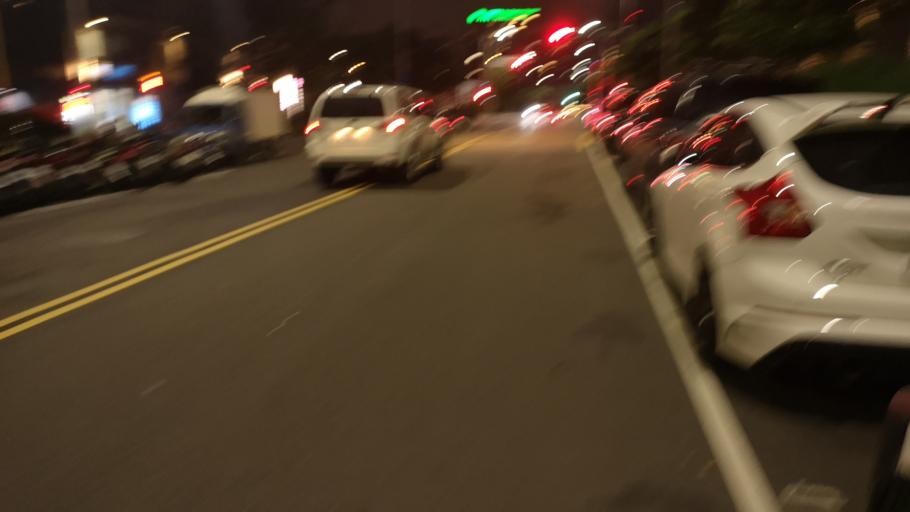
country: TW
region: Taipei
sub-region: Taipei
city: Banqiao
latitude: 24.9991
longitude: 121.4477
